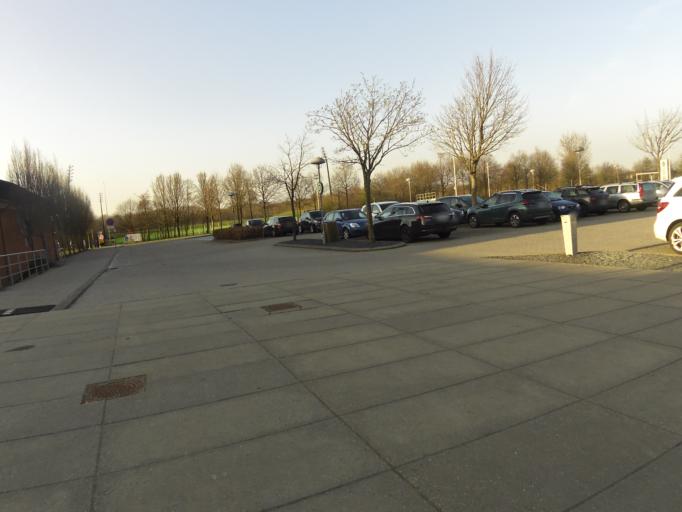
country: DK
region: South Denmark
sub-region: Vejen Kommune
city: Vejen
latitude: 55.4746
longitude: 9.1209
